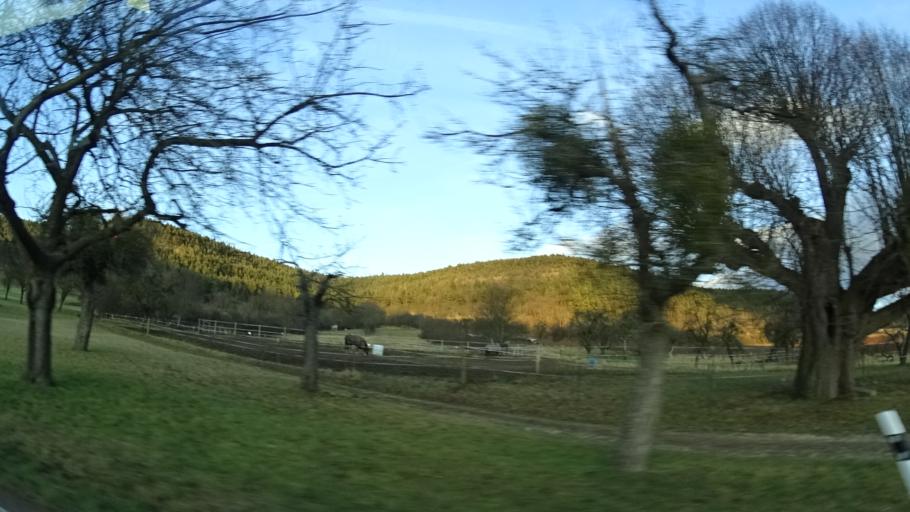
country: DE
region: Thuringia
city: Reinstadt
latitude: 50.7934
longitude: 11.3971
